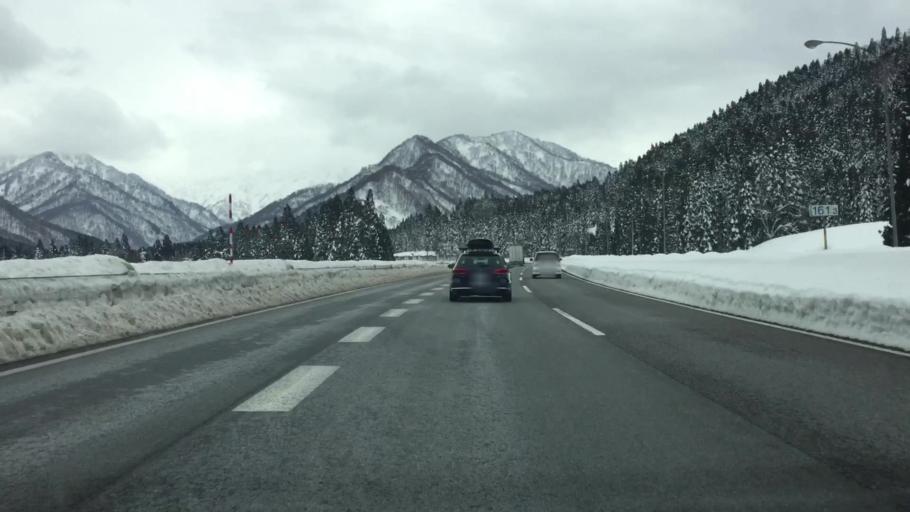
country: JP
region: Niigata
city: Shiozawa
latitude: 36.8902
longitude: 138.8481
